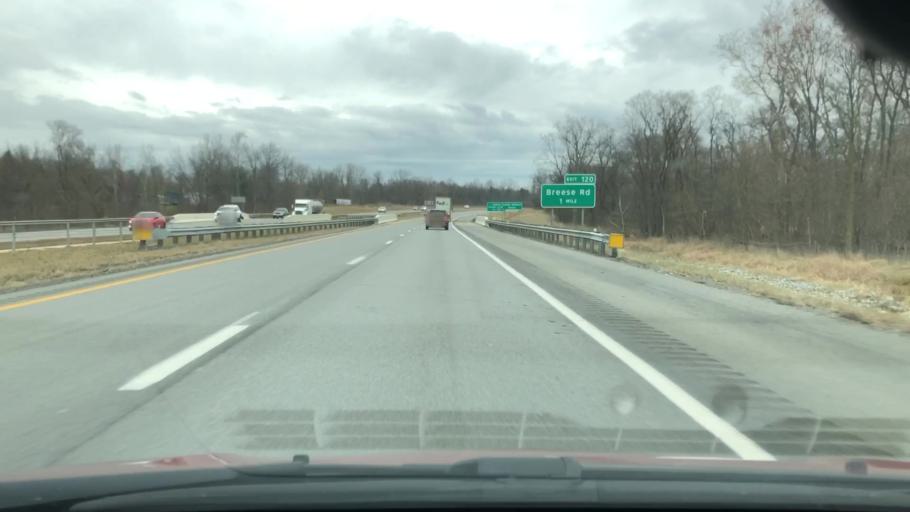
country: US
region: Ohio
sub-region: Allen County
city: Fort Shawnee
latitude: 40.6711
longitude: -84.1313
